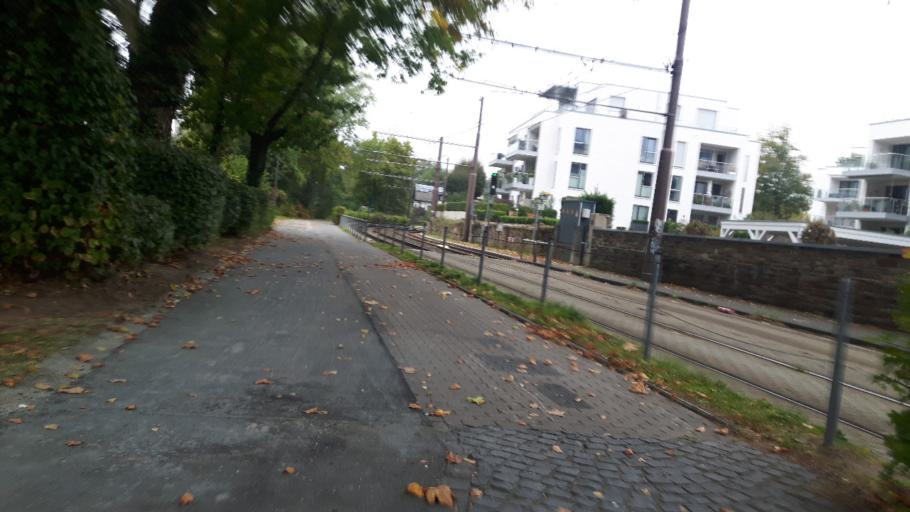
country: DE
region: North Rhine-Westphalia
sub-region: Regierungsbezirk Koln
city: Konigswinter
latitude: 50.6826
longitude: 7.1844
